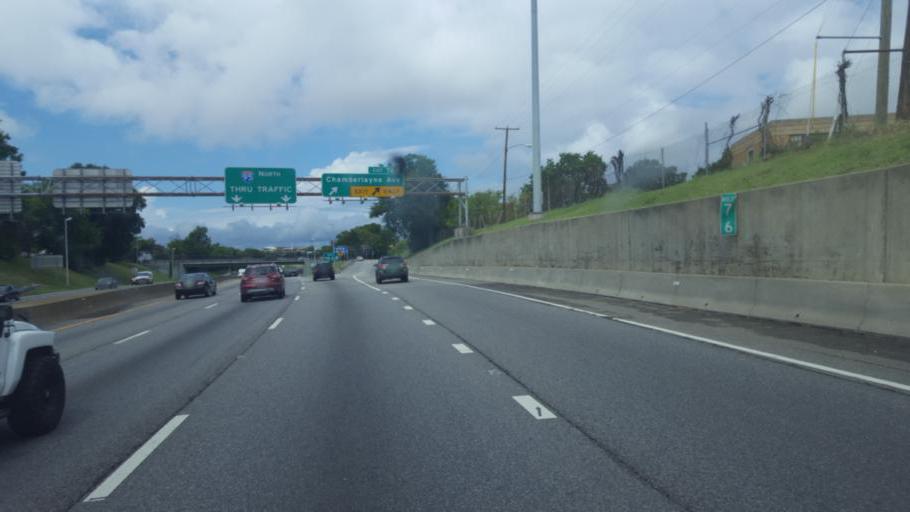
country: US
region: Virginia
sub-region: City of Richmond
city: Richmond
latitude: 37.5510
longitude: -77.4380
